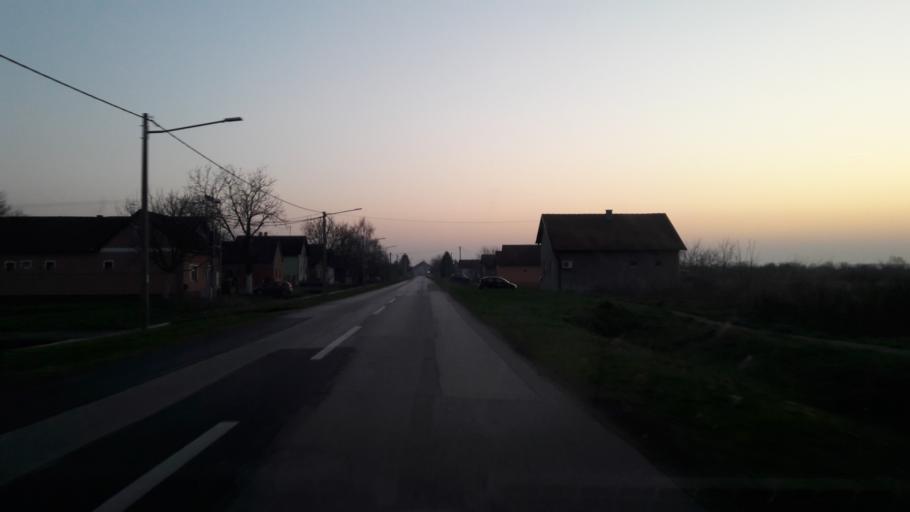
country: HR
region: Vukovarsko-Srijemska
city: Nijemci
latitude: 45.1876
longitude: 19.0156
